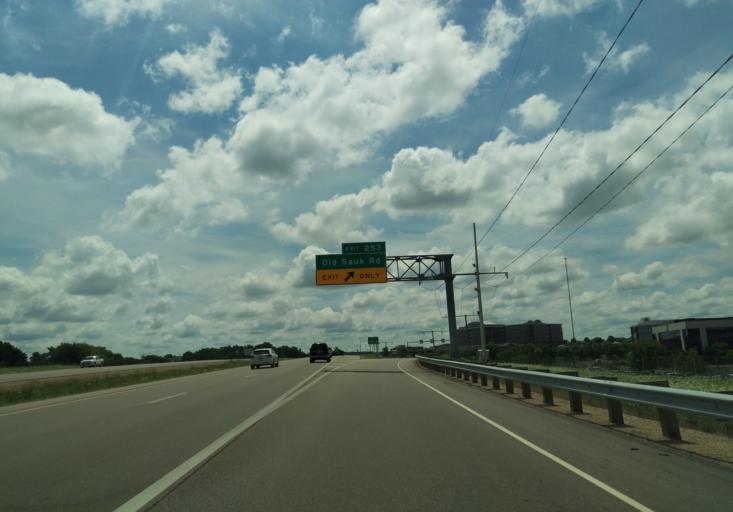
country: US
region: Wisconsin
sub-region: Dane County
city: Middleton
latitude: 43.0784
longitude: -89.5219
